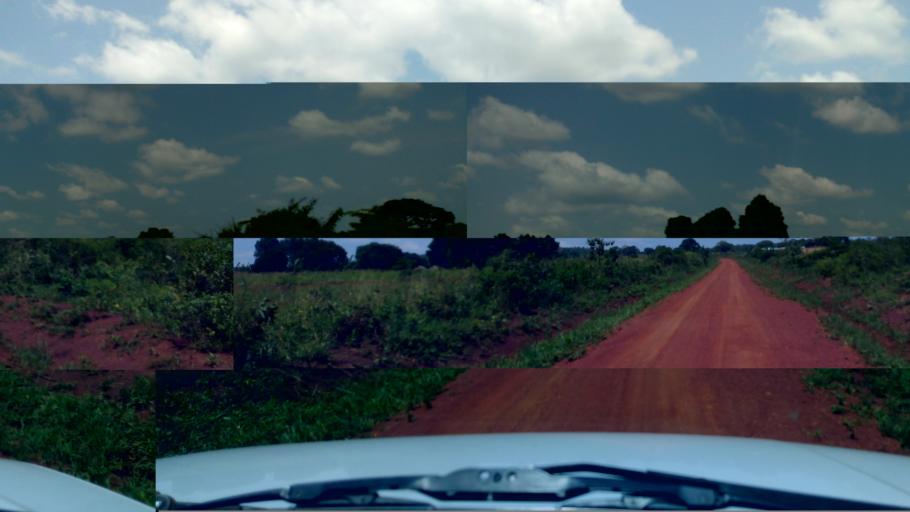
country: UG
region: Western Region
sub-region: Masindi District
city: Masindi
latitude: 1.7331
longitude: 31.8828
